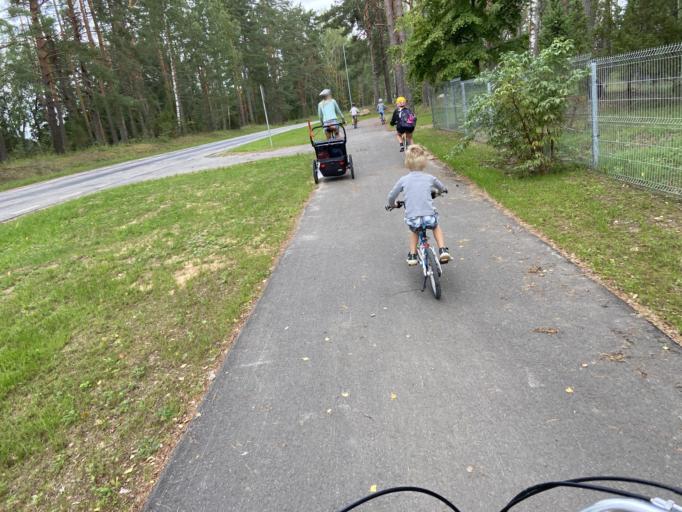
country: RU
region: Pskov
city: Pechory
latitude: 57.9399
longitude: 27.6521
